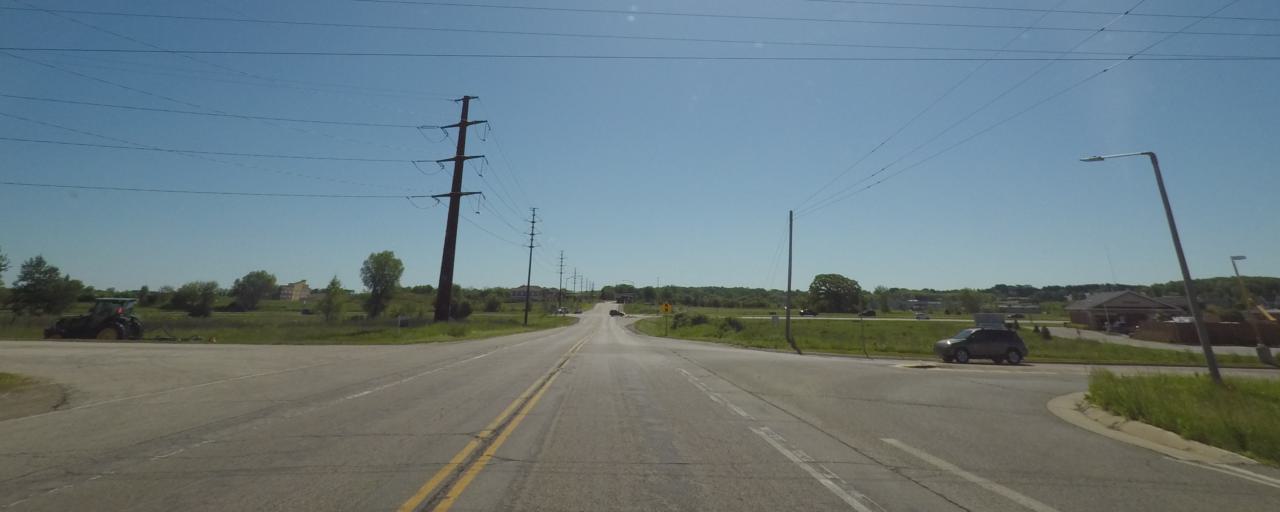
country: US
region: Wisconsin
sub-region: Dane County
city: Verona
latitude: 42.9724
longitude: -89.5142
